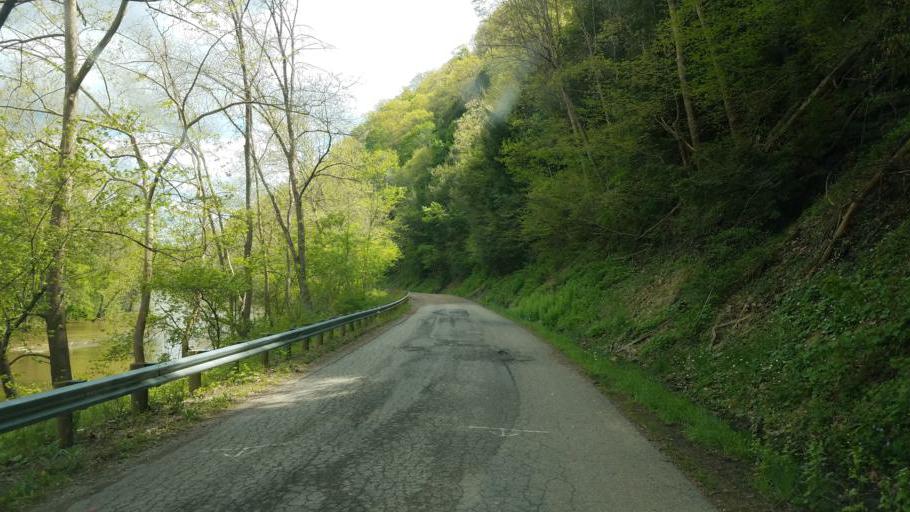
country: US
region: Ohio
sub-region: Ashland County
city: Loudonville
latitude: 40.5416
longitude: -82.2087
